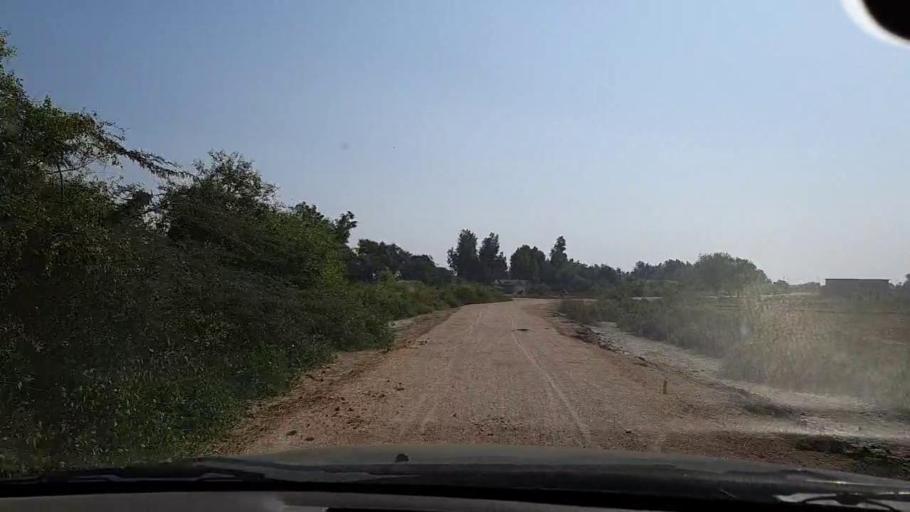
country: PK
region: Sindh
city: Chuhar Jamali
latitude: 24.3980
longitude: 67.8239
